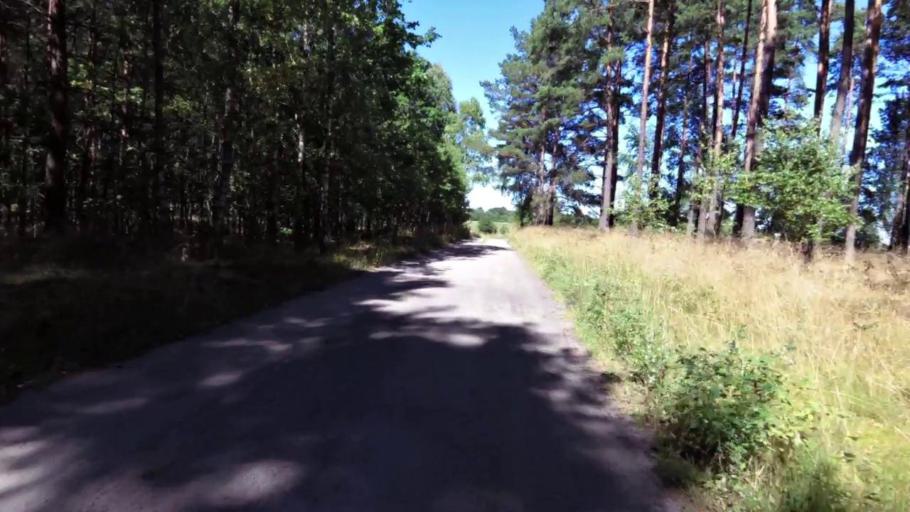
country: PL
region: West Pomeranian Voivodeship
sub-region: Powiat szczecinecki
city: Borne Sulinowo
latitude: 53.6678
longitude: 16.5603
